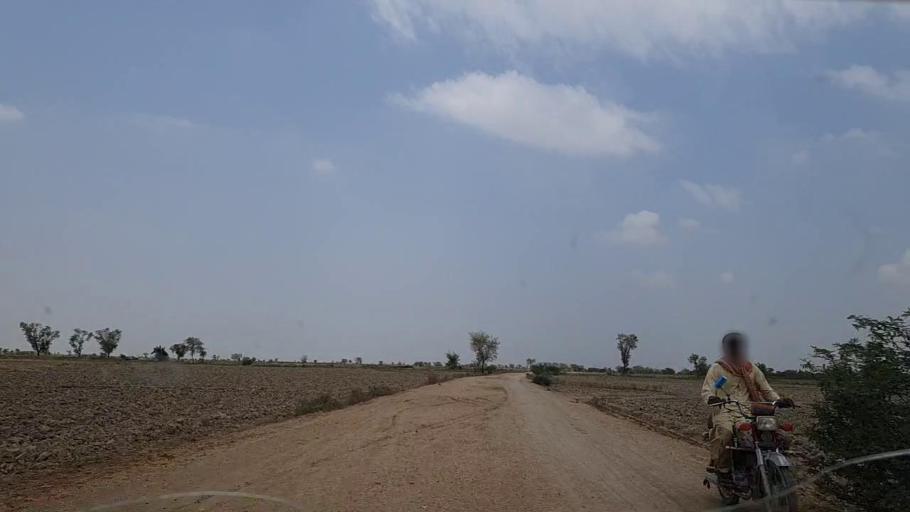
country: PK
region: Sindh
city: Phulji
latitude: 26.8240
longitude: 67.6402
